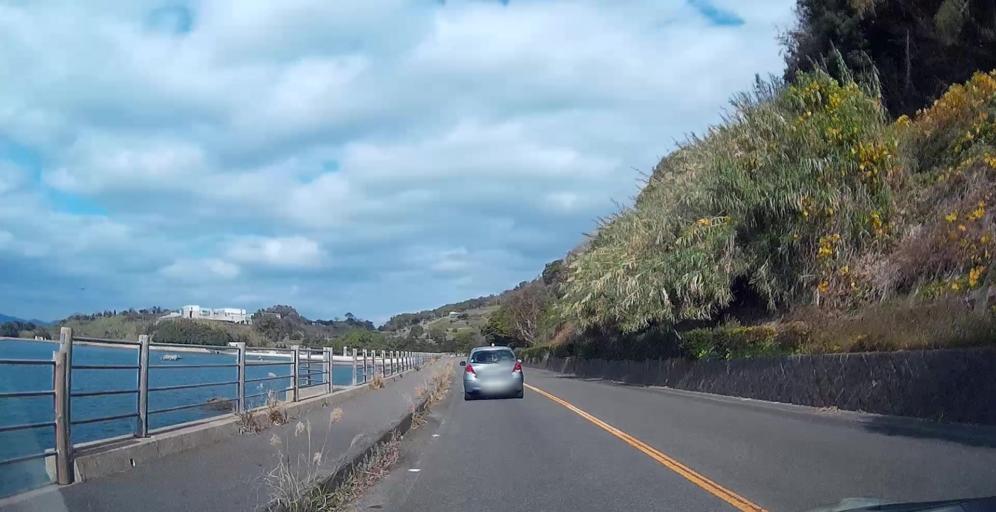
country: JP
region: Kumamoto
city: Minamata
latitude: 32.3150
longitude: 130.4712
